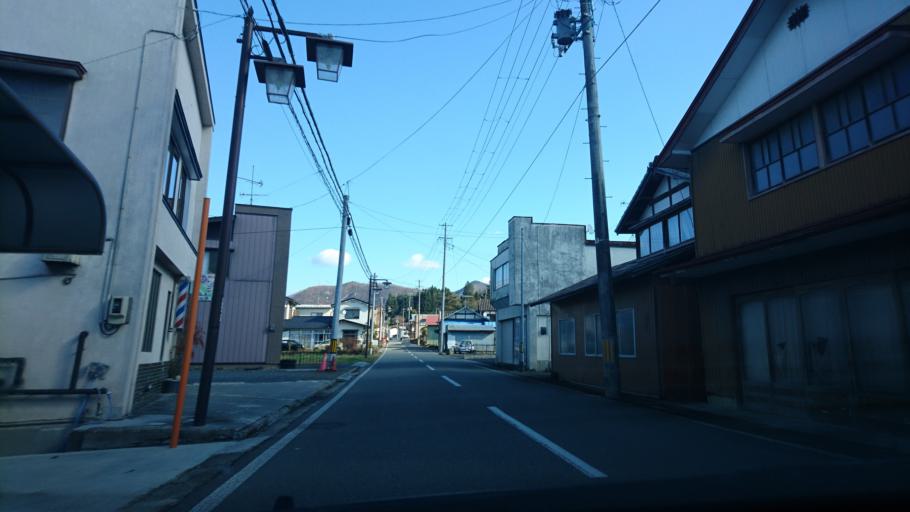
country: JP
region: Iwate
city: Ichinoseki
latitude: 39.0176
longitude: 141.4045
